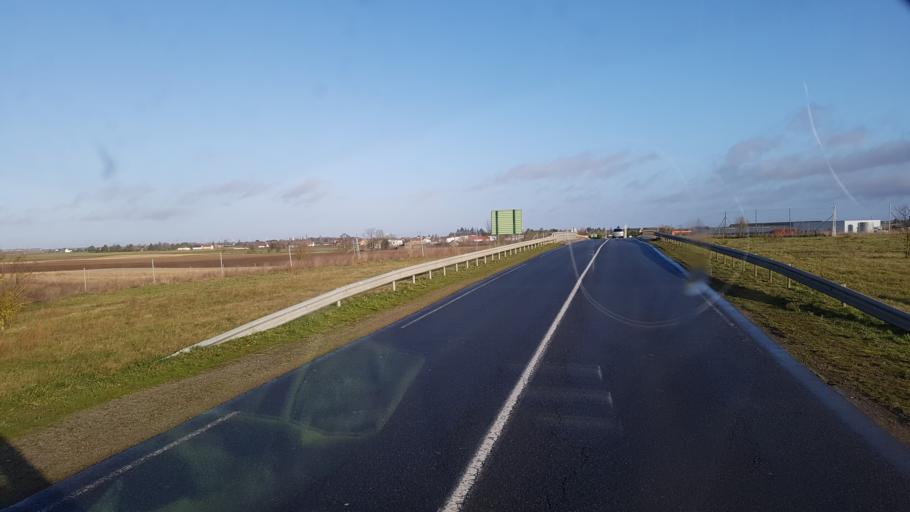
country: FR
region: Centre
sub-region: Departement du Loiret
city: Dadonville
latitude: 48.1118
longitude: 2.2483
